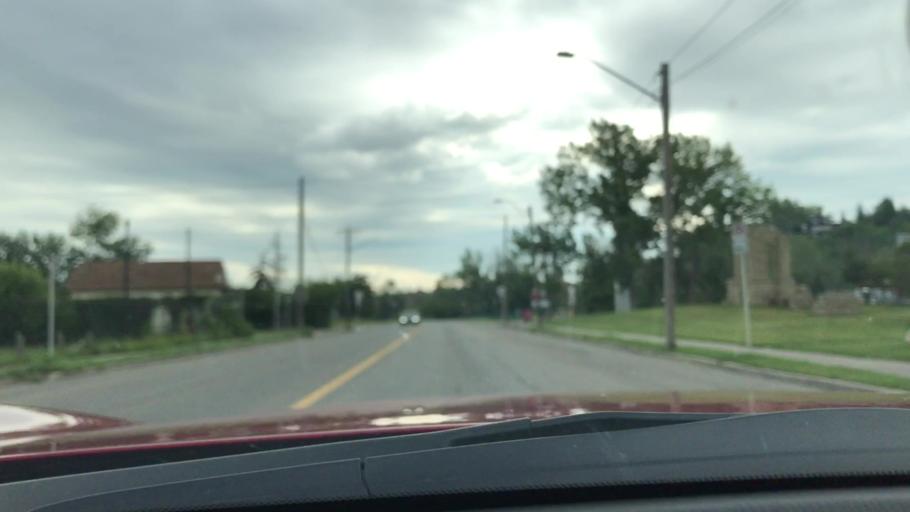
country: CA
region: Alberta
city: Calgary
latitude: 51.0410
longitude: -114.0497
